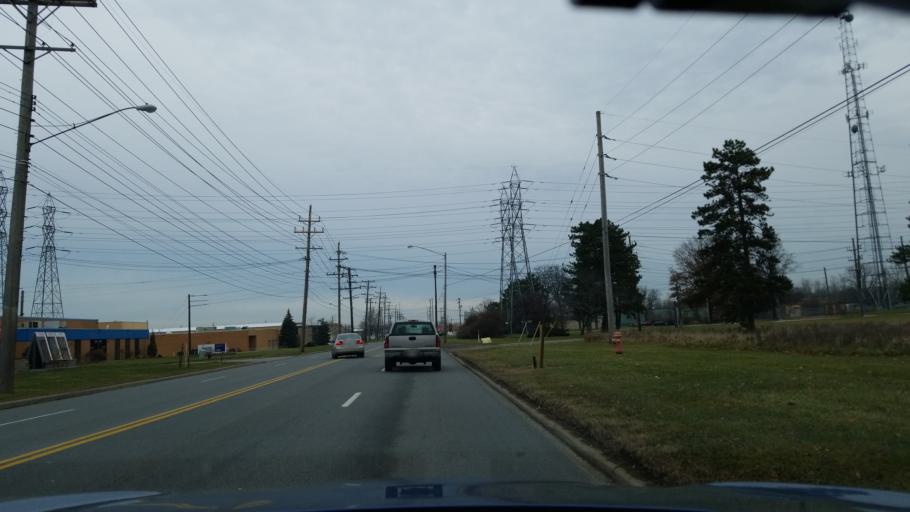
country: US
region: Ohio
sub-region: Summit County
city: Northfield
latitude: 41.3611
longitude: -81.5267
